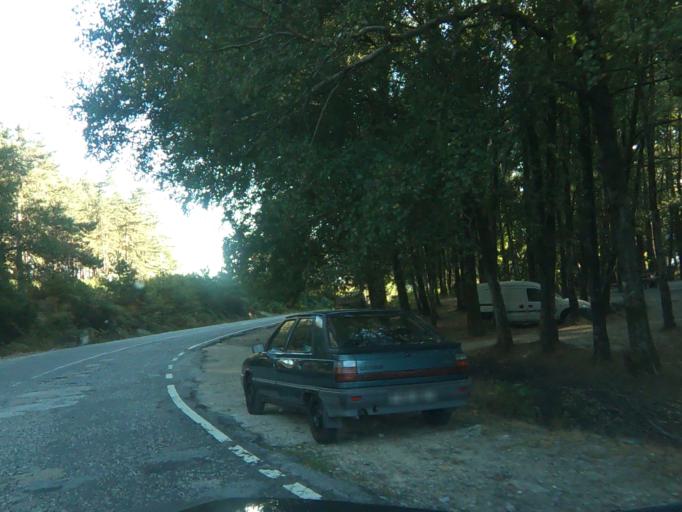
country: PT
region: Vila Real
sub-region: Vila Real
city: Vila Real
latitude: 41.3488
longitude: -7.7904
